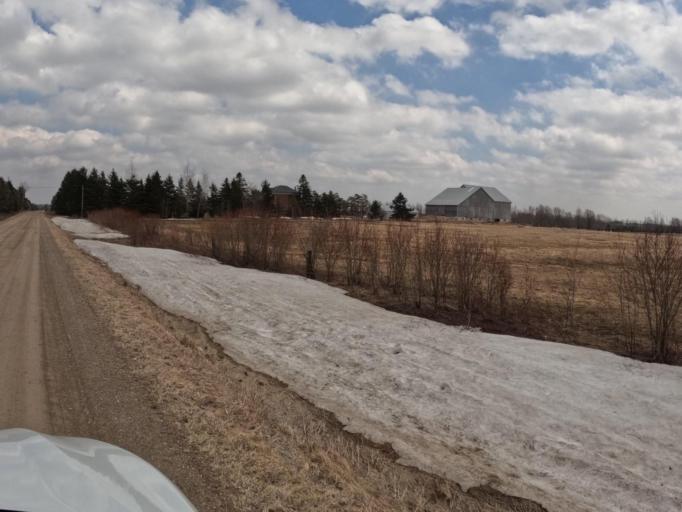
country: CA
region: Ontario
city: Shelburne
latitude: 44.0265
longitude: -80.2679
